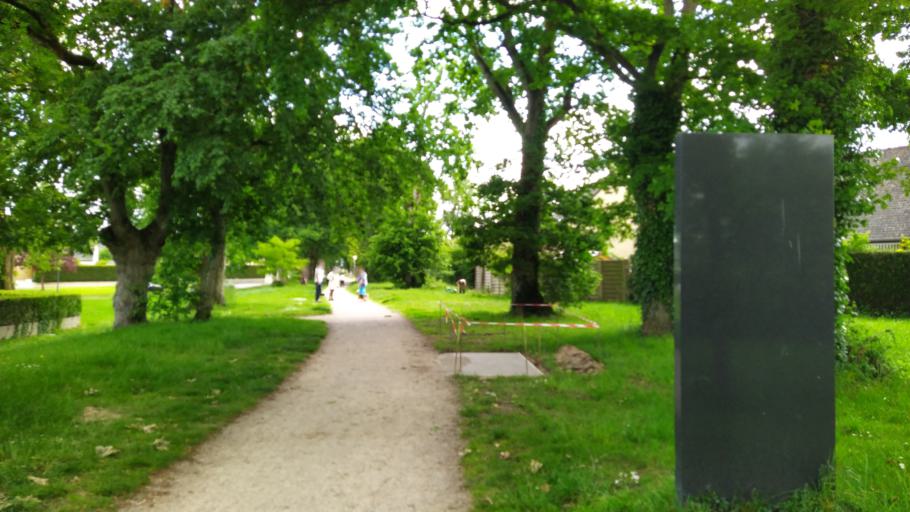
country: FR
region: Brittany
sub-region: Departement d'Ille-et-Vilaine
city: Liffre
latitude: 48.2084
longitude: -1.5130
